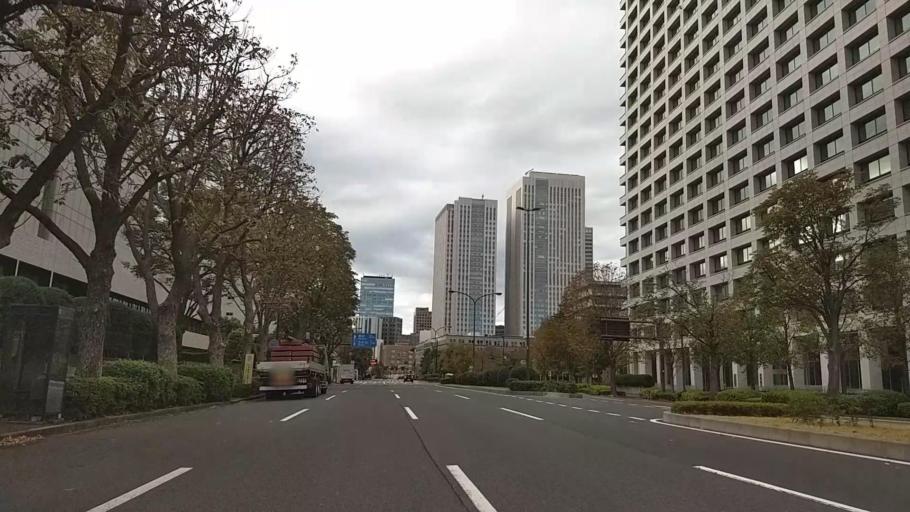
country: JP
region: Tokyo
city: Tokyo
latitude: 35.6757
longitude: 139.7524
